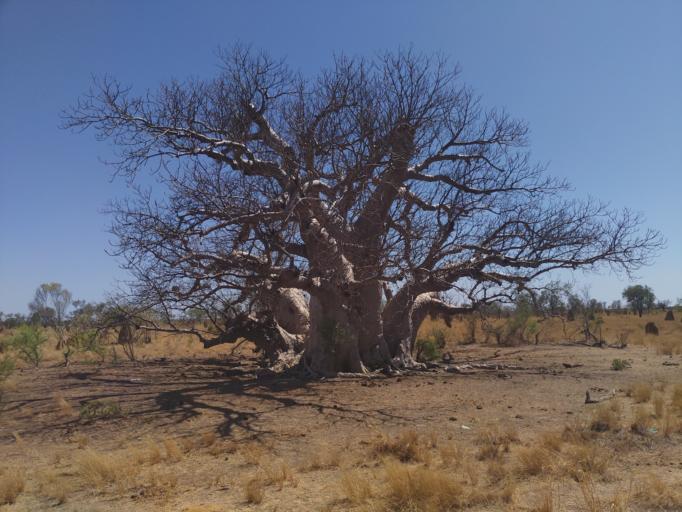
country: AU
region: Western Australia
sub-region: Derby-West Kimberley
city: Derby
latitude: -17.6713
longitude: 123.3990
